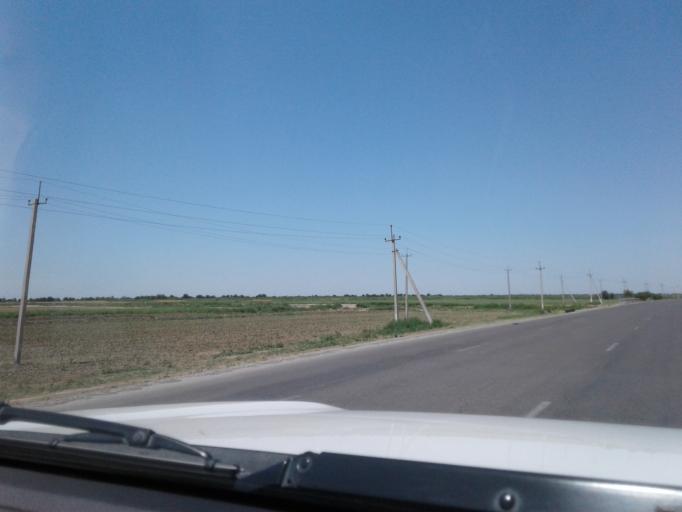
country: TM
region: Mary
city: Bayramaly
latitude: 37.6050
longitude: 62.2443
